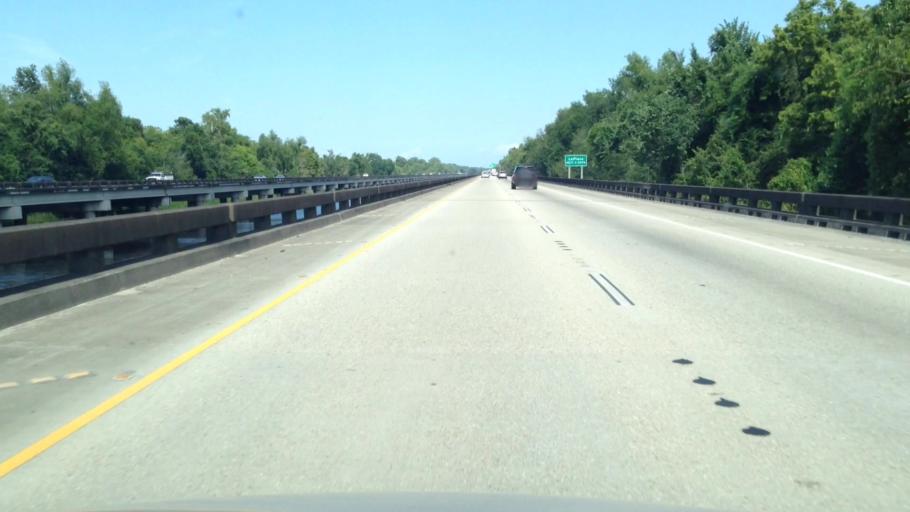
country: US
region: Louisiana
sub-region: Saint John the Baptist Parish
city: Montegut
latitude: 30.1096
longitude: -90.5313
